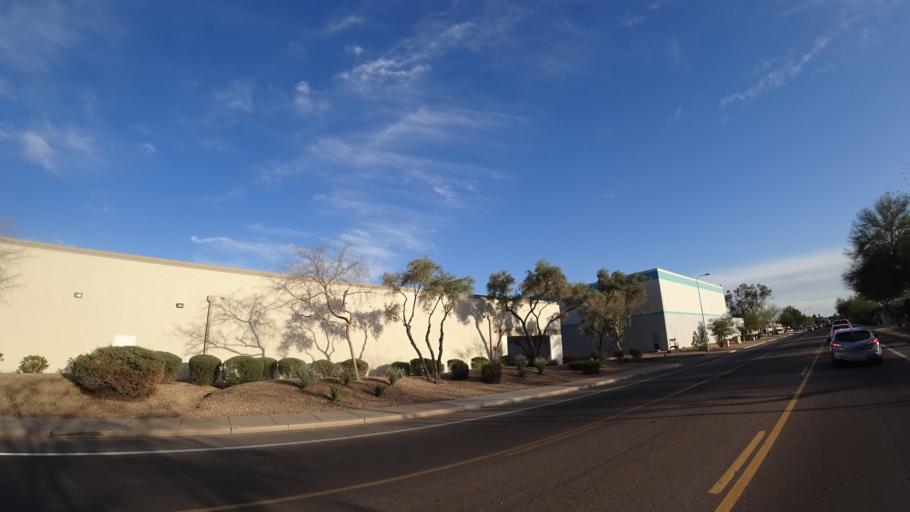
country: US
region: Arizona
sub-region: Maricopa County
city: Tempe Junction
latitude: 33.4023
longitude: -111.9522
